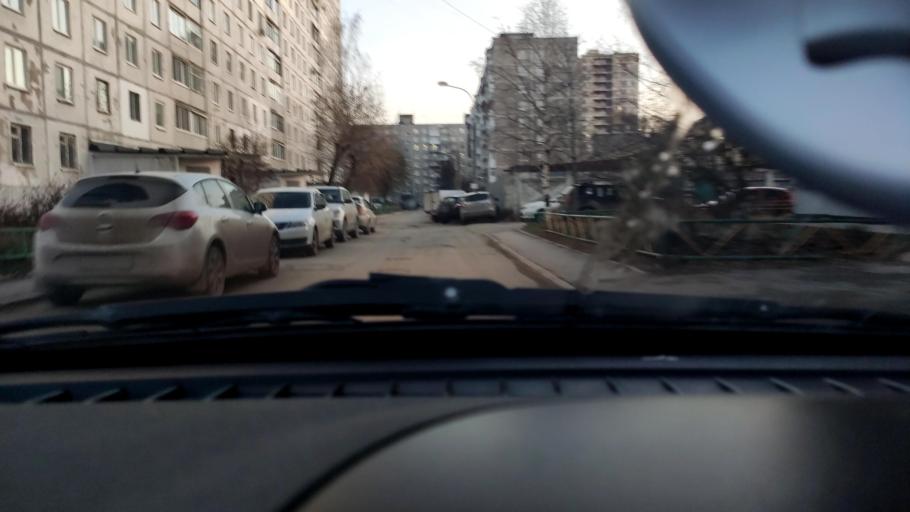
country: RU
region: Perm
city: Kondratovo
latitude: 57.9969
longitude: 56.1574
